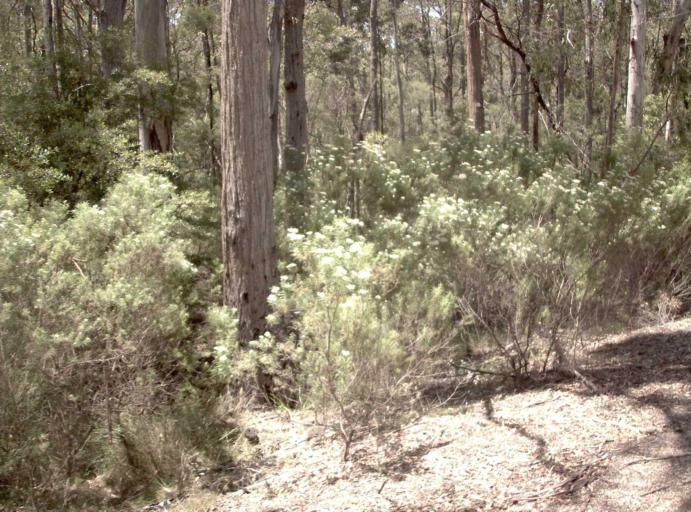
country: AU
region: Victoria
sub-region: East Gippsland
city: Lakes Entrance
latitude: -37.6315
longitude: 147.8904
